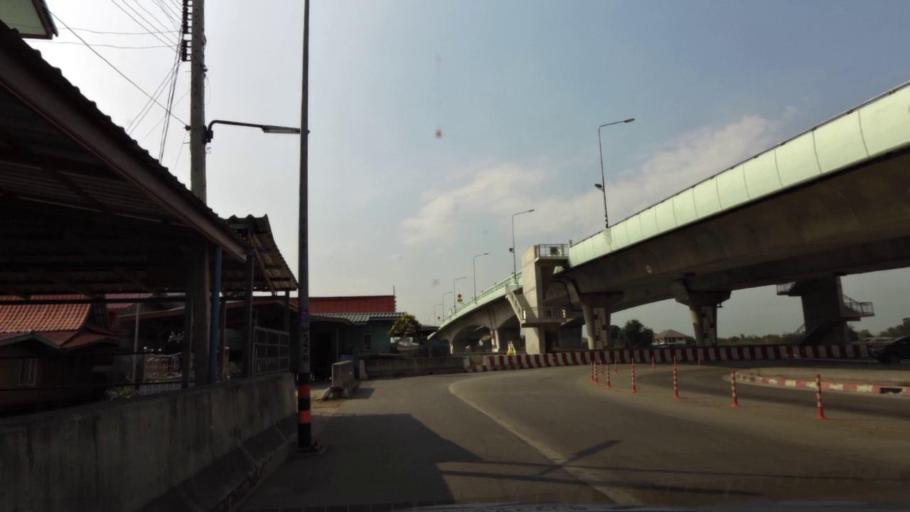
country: TH
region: Phra Nakhon Si Ayutthaya
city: Phra Nakhon Si Ayutthaya
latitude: 14.3307
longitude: 100.5784
